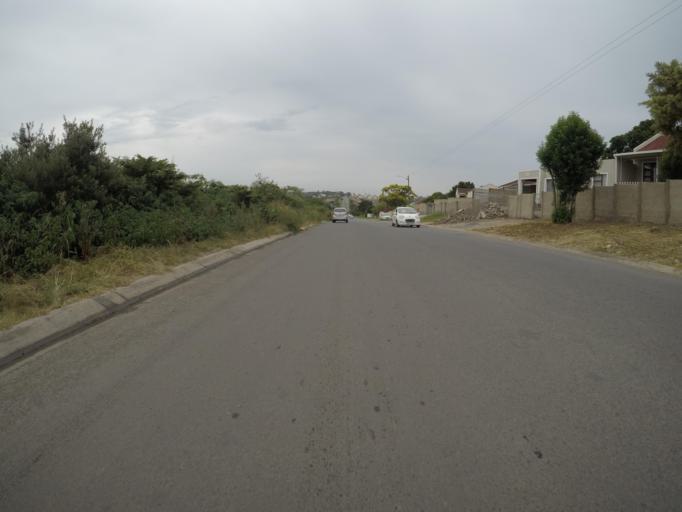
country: ZA
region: Eastern Cape
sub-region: Buffalo City Metropolitan Municipality
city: East London
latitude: -33.0049
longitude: 27.8560
